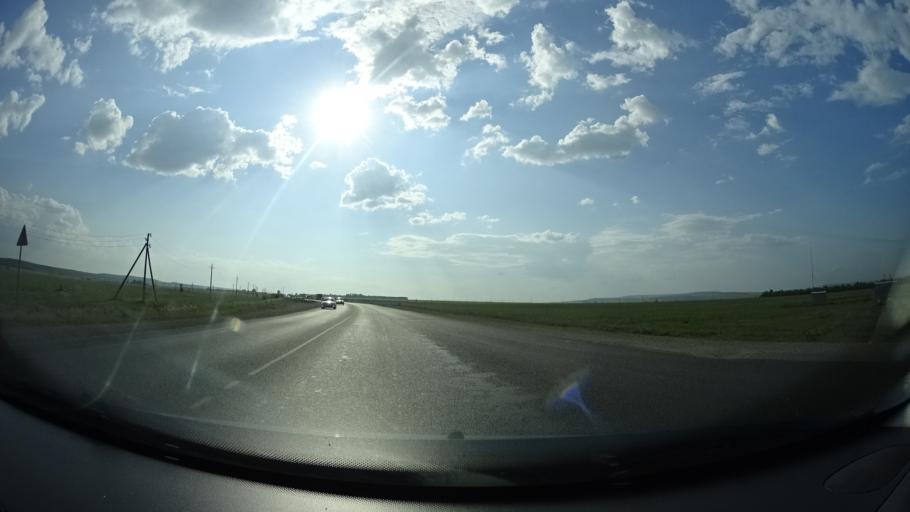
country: RU
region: Bashkortostan
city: Oktyabr'skiy
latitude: 54.4821
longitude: 53.3843
